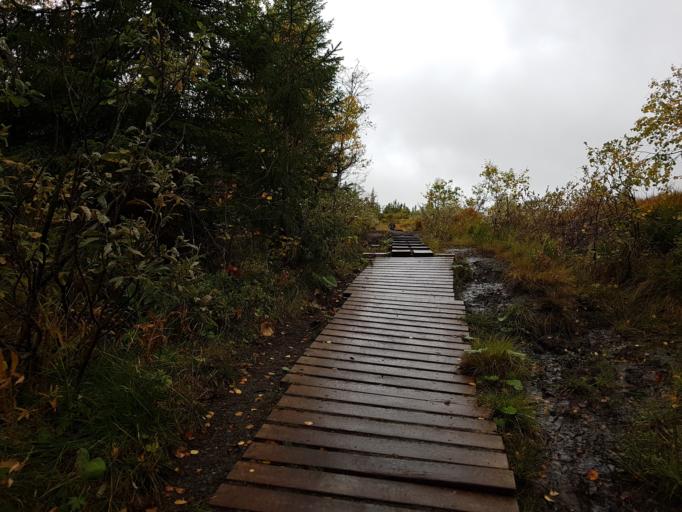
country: NO
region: Sor-Trondelag
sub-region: Melhus
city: Melhus
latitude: 63.4150
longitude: 10.2230
